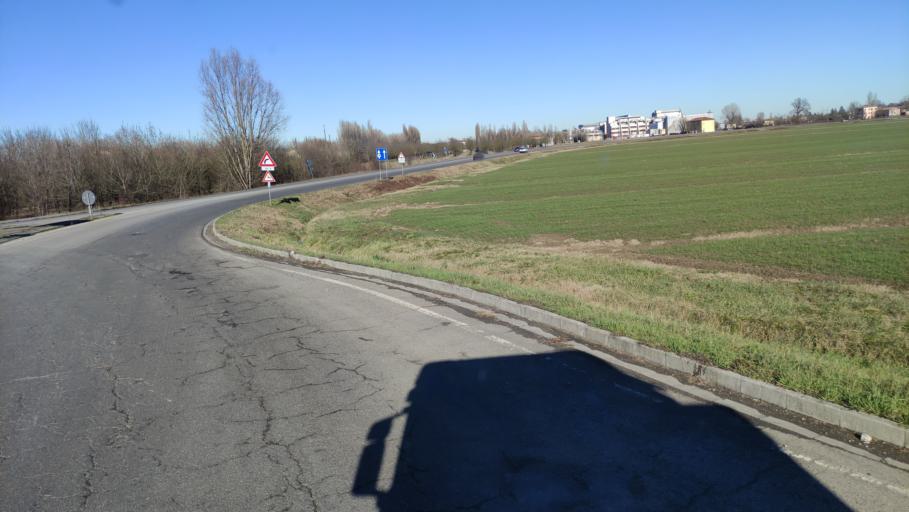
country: IT
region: Emilia-Romagna
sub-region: Provincia di Reggio Emilia
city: Correggio
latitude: 44.7590
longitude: 10.7941
